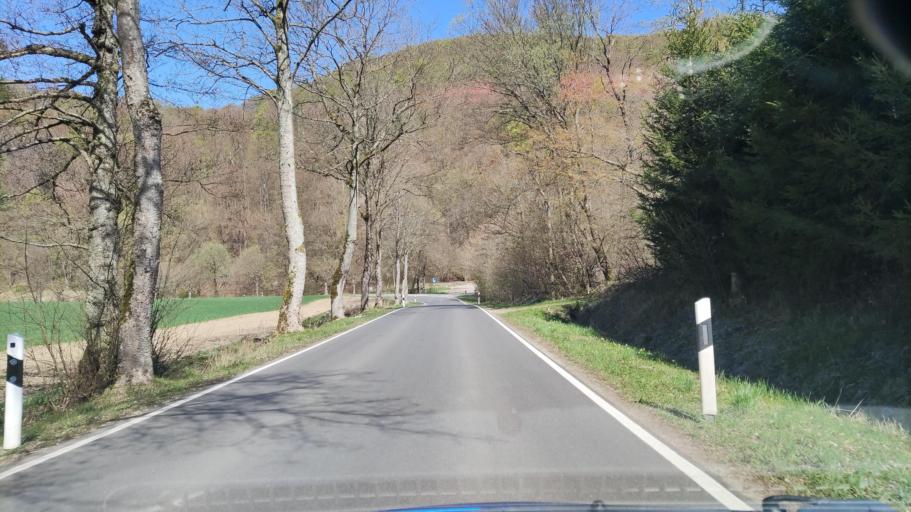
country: DE
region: Lower Saxony
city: Eimen
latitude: 51.9127
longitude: 9.7780
